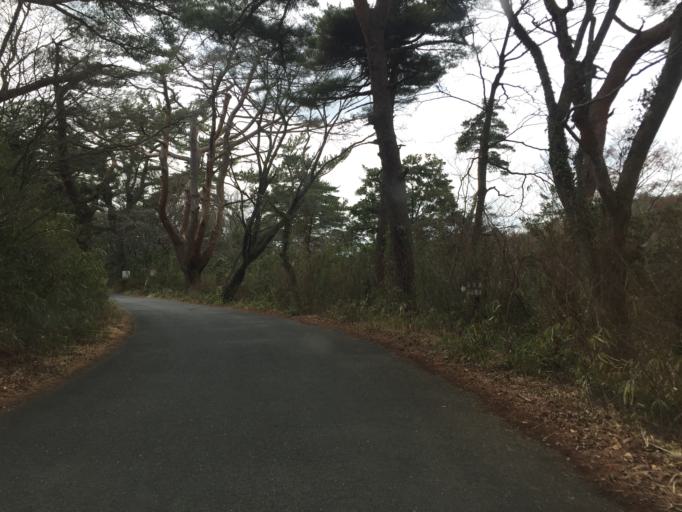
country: JP
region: Ibaraki
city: Kitaibaraki
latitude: 36.8697
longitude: 140.7814
